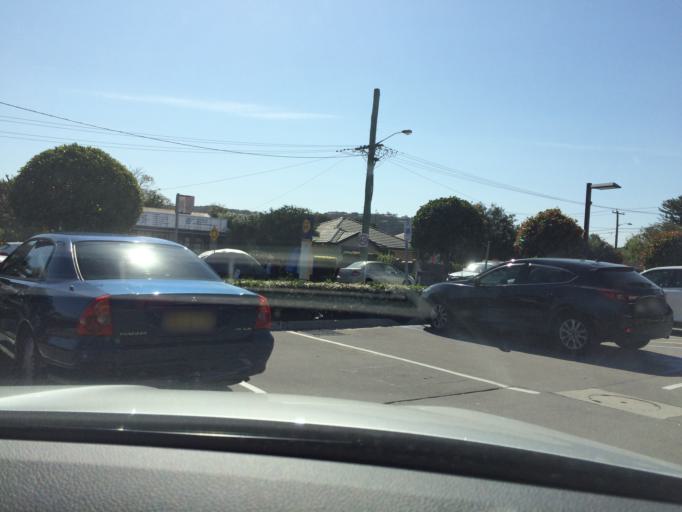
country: AU
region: New South Wales
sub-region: Gosford Shire
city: Umina
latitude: -33.5204
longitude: 151.3171
